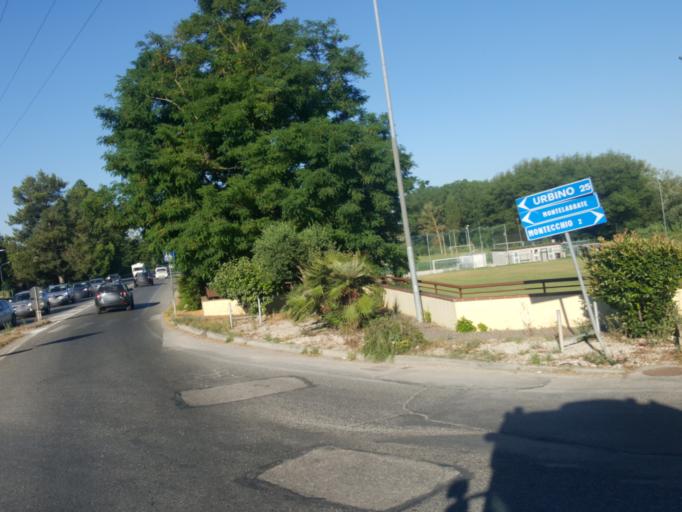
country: IT
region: The Marches
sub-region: Provincia di Pesaro e Urbino
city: Montelabbate
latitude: 43.8511
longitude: 12.7877
